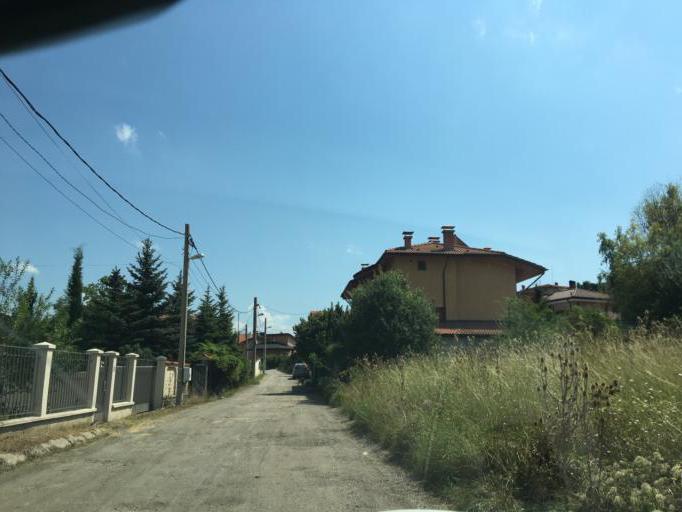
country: BG
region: Sofiya
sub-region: Obshtina Elin Pelin
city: Elin Pelin
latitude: 42.6042
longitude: 23.4676
